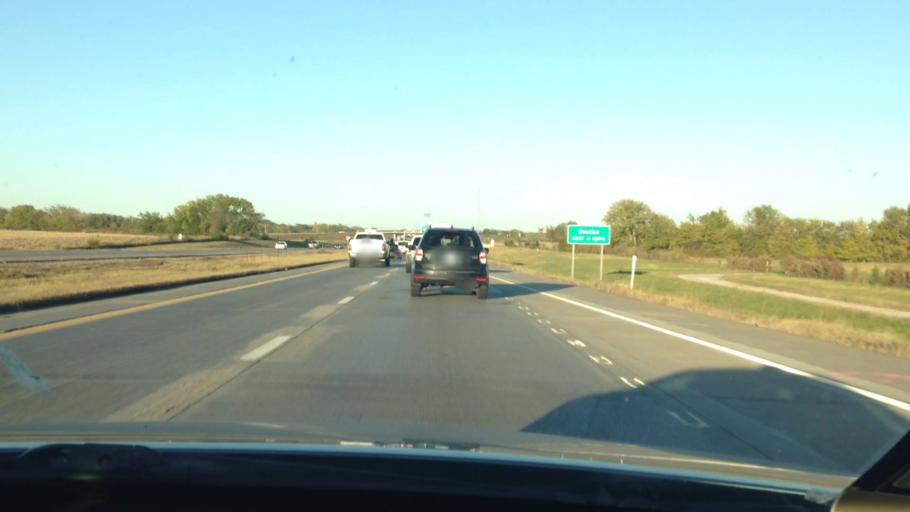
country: US
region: Kansas
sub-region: Johnson County
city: Olathe
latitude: 38.8341
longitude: -94.8486
